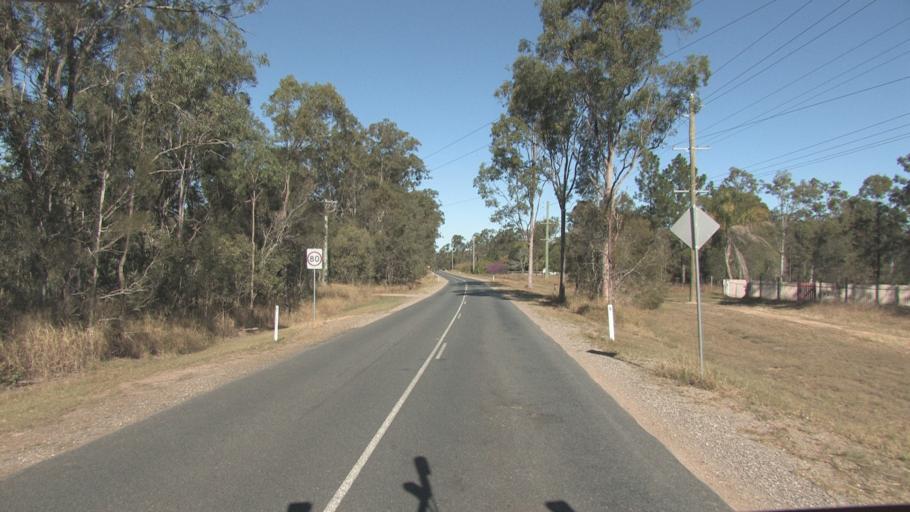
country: AU
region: Queensland
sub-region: Logan
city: North Maclean
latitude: -27.7613
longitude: 152.9963
